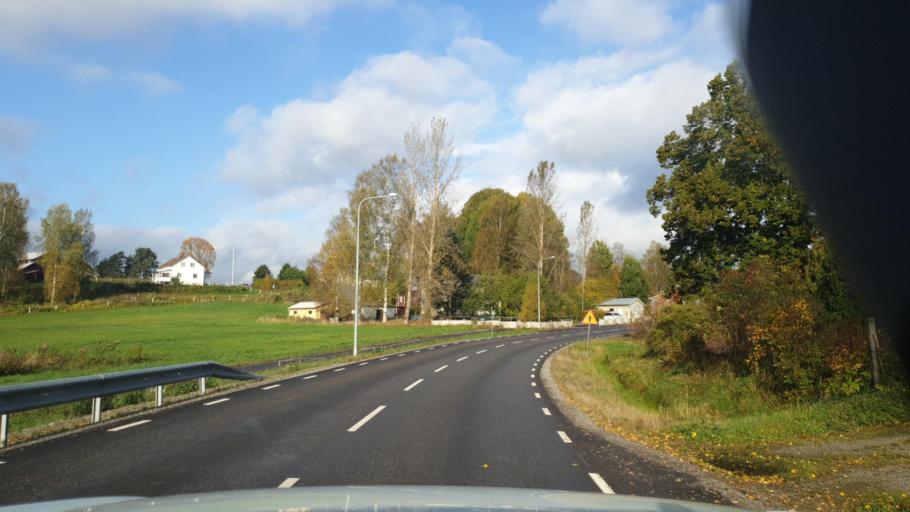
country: SE
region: Vaermland
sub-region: Arvika Kommun
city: Arvika
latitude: 59.5488
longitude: 12.5634
